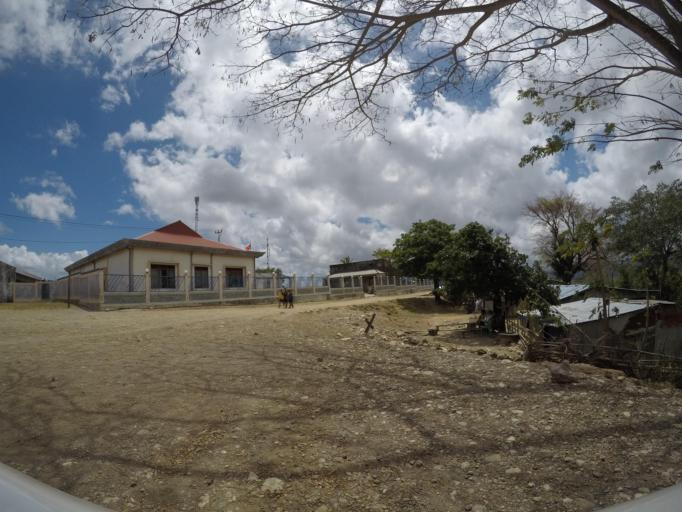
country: TL
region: Lautem
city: Lospalos
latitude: -8.5425
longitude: 126.8341
